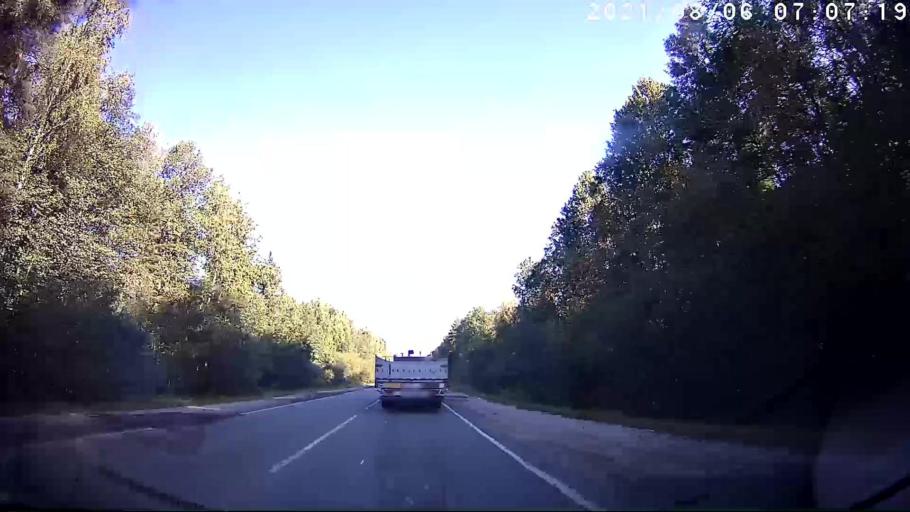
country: RU
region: Mariy-El
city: Yoshkar-Ola
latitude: 56.5626
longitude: 47.9794
